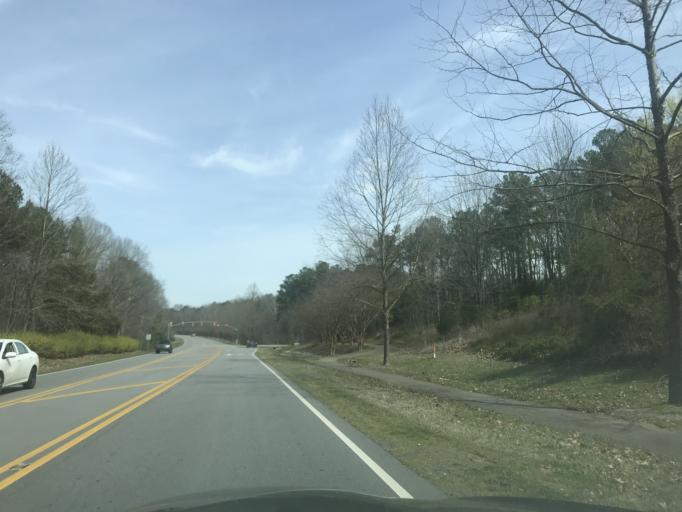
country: US
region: North Carolina
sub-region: Wake County
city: Morrisville
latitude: 35.8877
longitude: -78.8816
